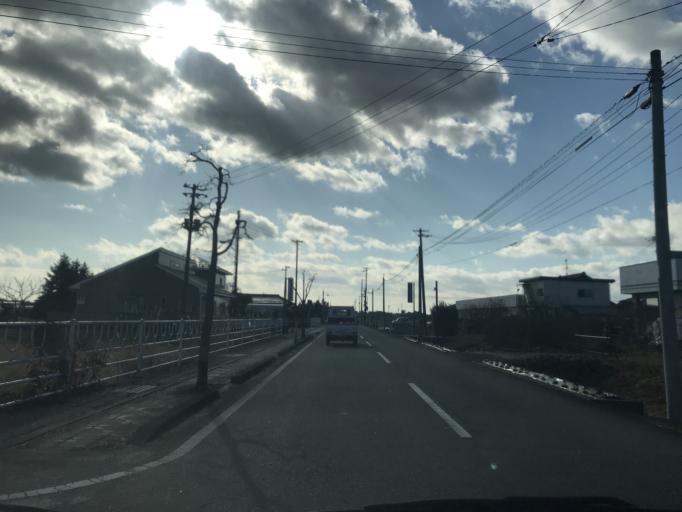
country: JP
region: Iwate
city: Ichinoseki
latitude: 38.7526
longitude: 141.0665
